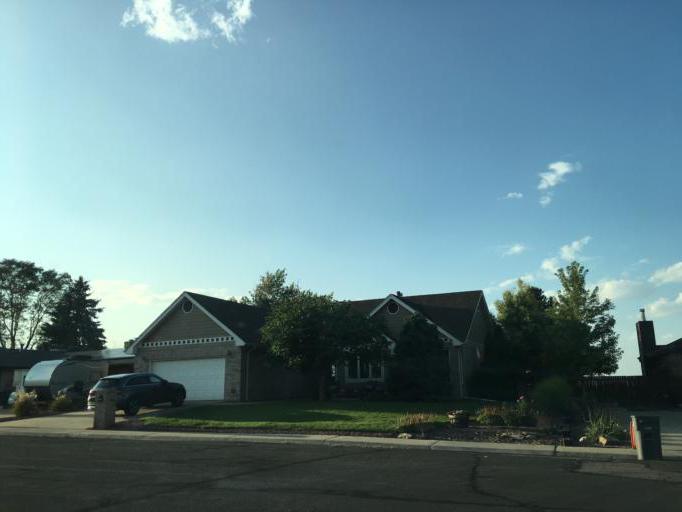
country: US
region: Colorado
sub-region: Jefferson County
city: Applewood
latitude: 39.7942
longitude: -105.1504
